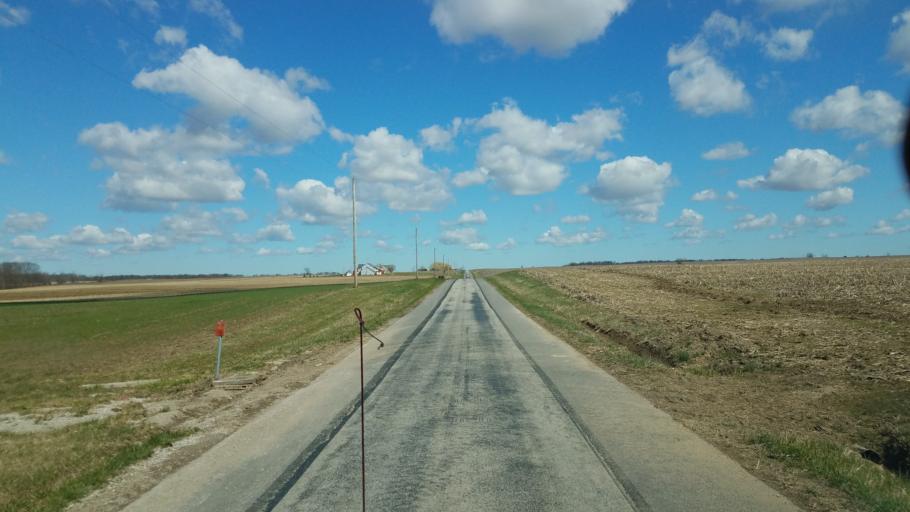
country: US
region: Ohio
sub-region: Sandusky County
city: Mount Carmel
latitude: 41.0823
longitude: -82.9382
